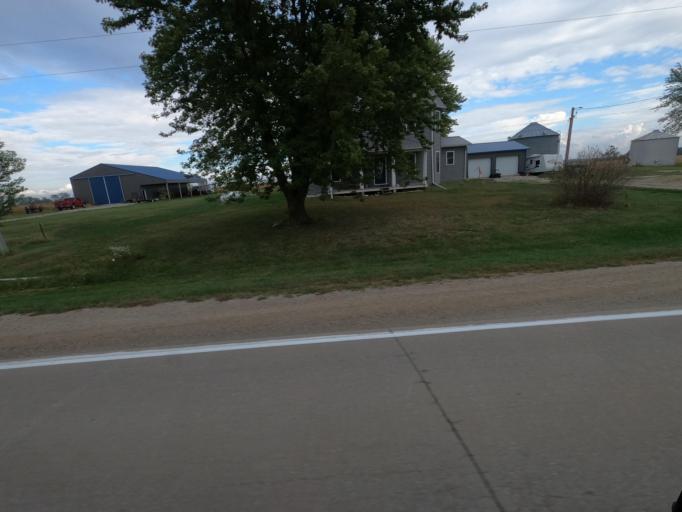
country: US
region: Iowa
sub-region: Henry County
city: Mount Pleasant
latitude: 40.8018
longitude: -91.7042
